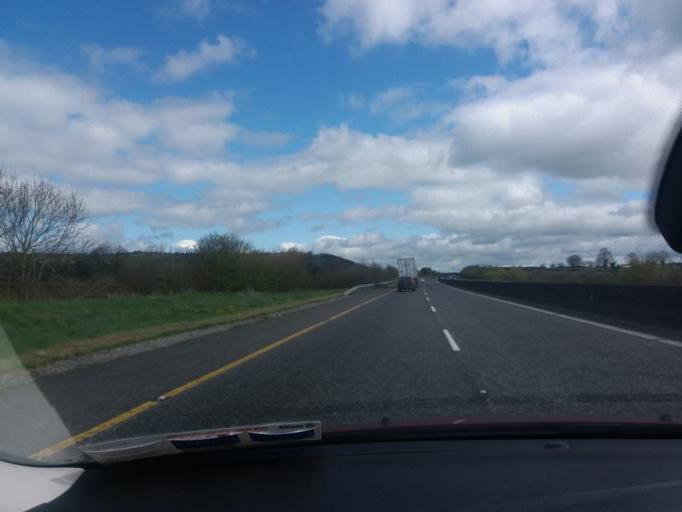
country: IE
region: Munster
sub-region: County Cork
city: Rathcormac
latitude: 52.0904
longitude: -8.2917
